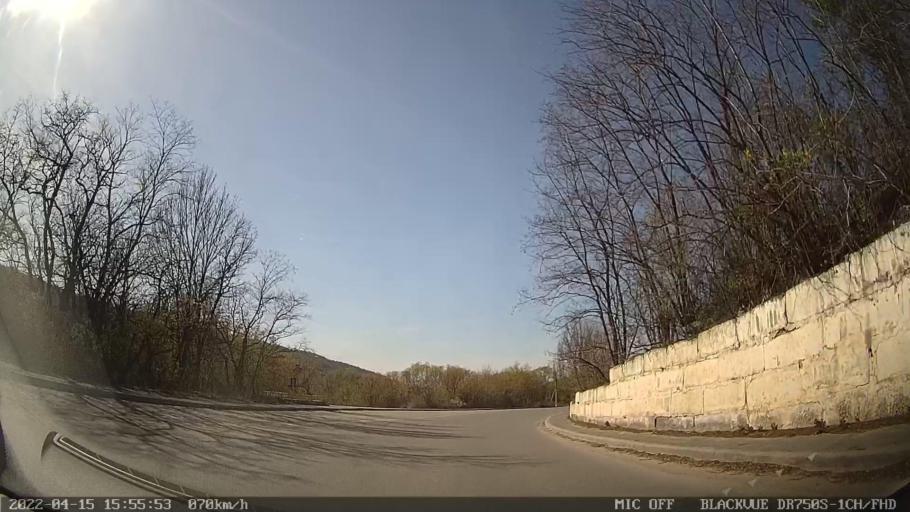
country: MD
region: Raionul Ocnita
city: Otaci
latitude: 48.4009
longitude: 27.8784
